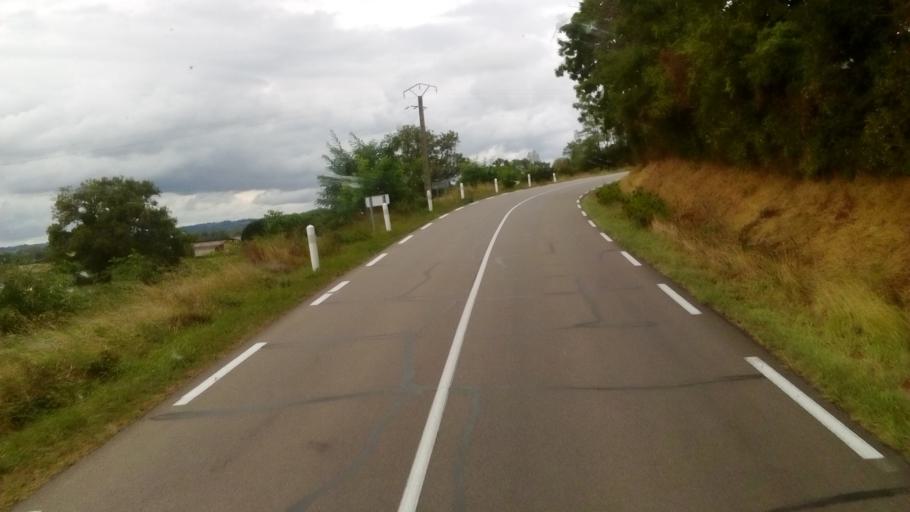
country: FR
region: Bourgogne
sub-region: Departement de Saone-et-Loire
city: Saint-Yan
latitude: 46.4408
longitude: 4.0180
